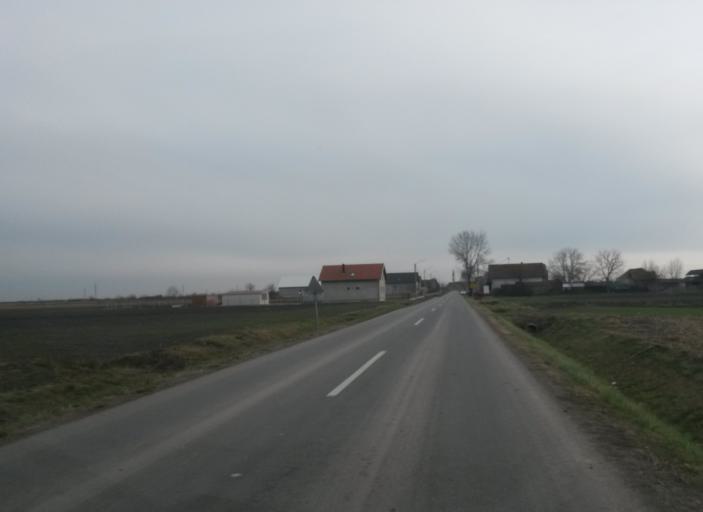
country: HR
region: Osjecko-Baranjska
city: Antunovac
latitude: 45.4919
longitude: 18.6253
